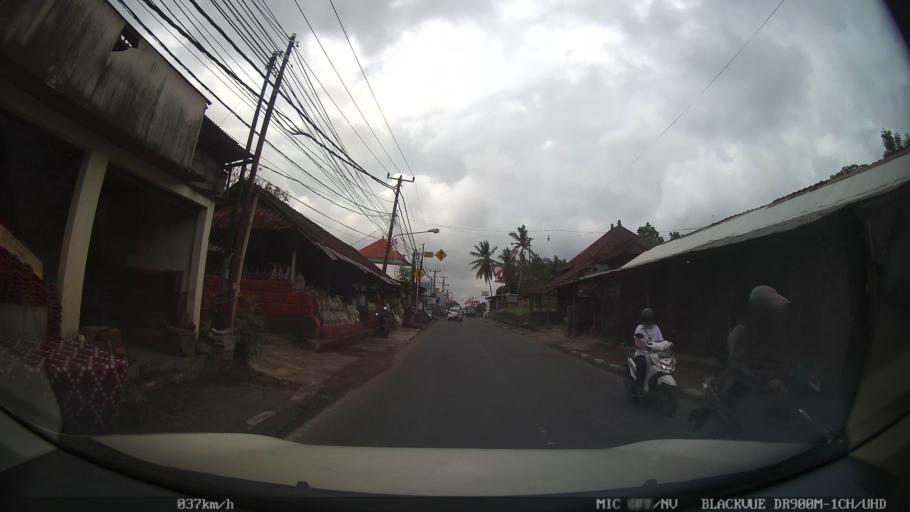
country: ID
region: Bali
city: Banjar Bucu
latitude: -8.5868
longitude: 115.2103
